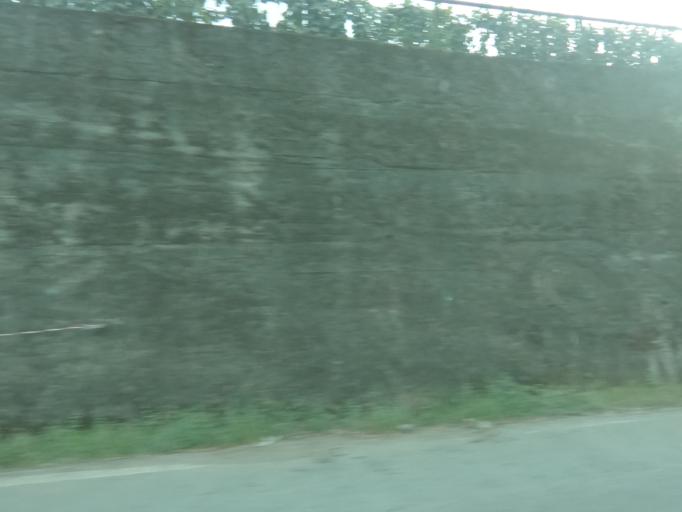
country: PT
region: Vila Real
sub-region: Mesao Frio
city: Mesao Frio
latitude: 41.1847
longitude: -7.8566
